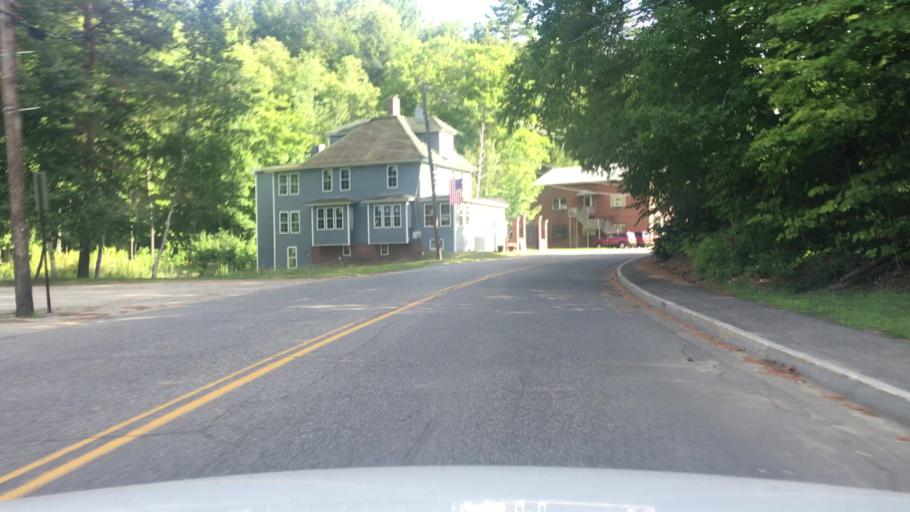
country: US
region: Maine
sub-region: Franklin County
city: Wilton
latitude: 44.5906
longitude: -70.2291
